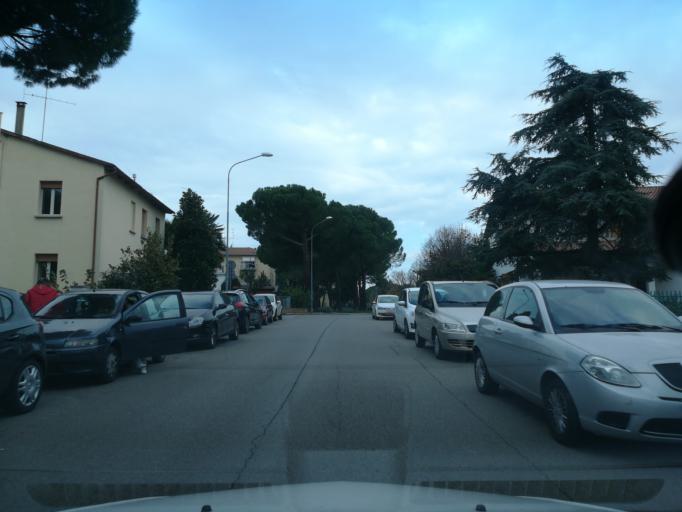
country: IT
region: Emilia-Romagna
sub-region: Provincia di Bologna
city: Imola
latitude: 44.3638
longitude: 11.6929
